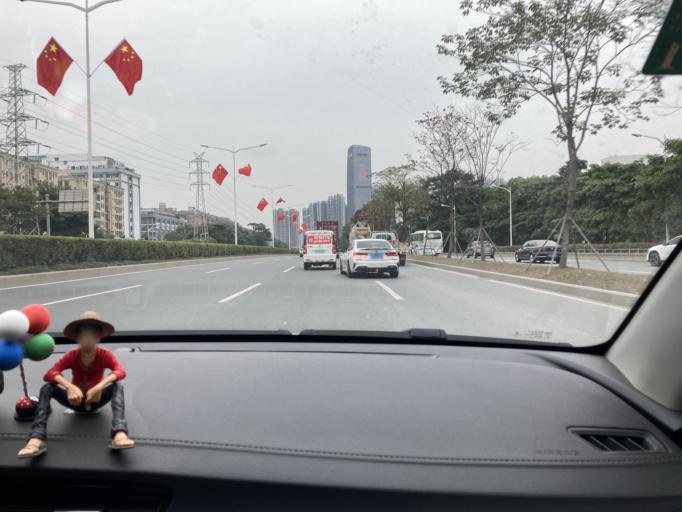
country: CN
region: Guangdong
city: Xin'an
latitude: 22.5554
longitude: 113.9265
